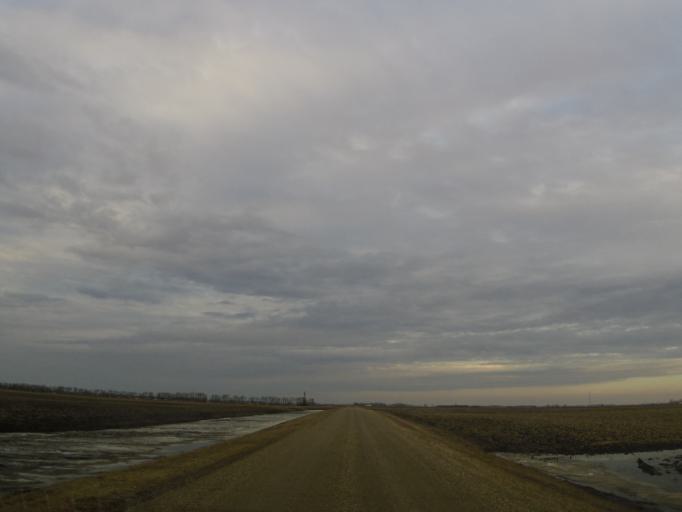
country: US
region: North Dakota
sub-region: Walsh County
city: Grafton
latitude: 48.3686
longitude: -97.2153
